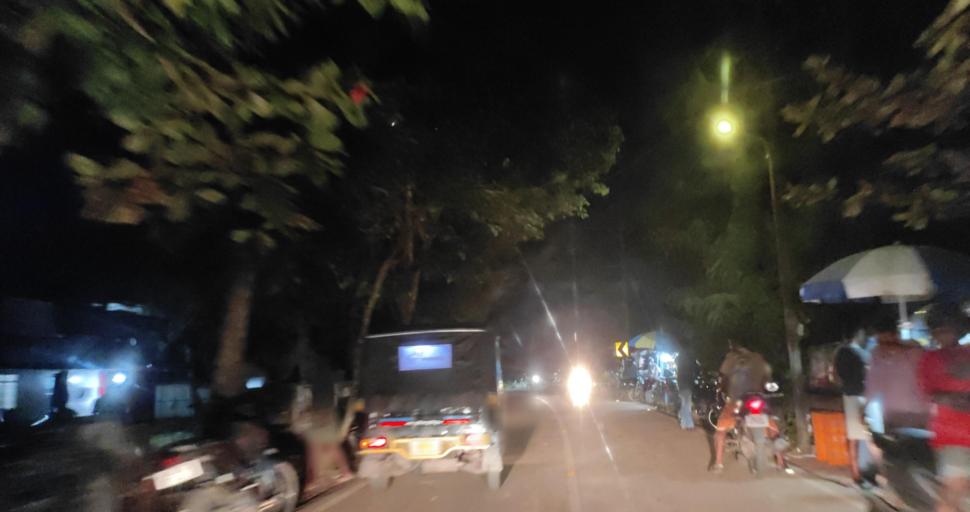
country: IN
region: Kerala
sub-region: Alappuzha
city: Vayalar
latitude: 9.7452
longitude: 76.2989
